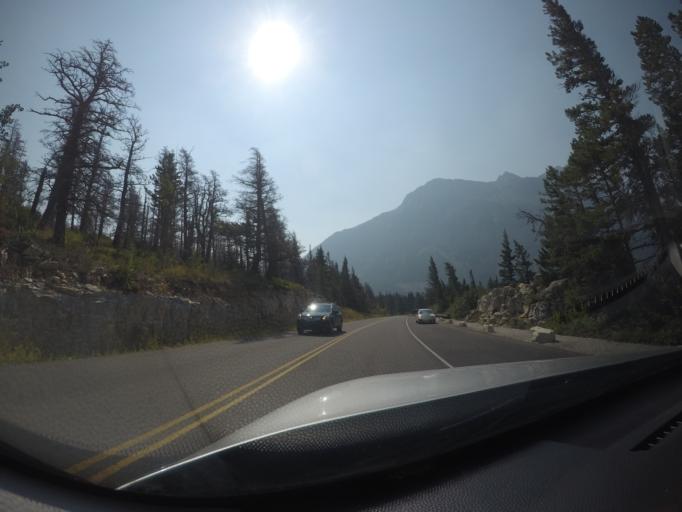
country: US
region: Montana
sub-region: Glacier County
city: Browning
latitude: 48.6944
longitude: -113.5323
